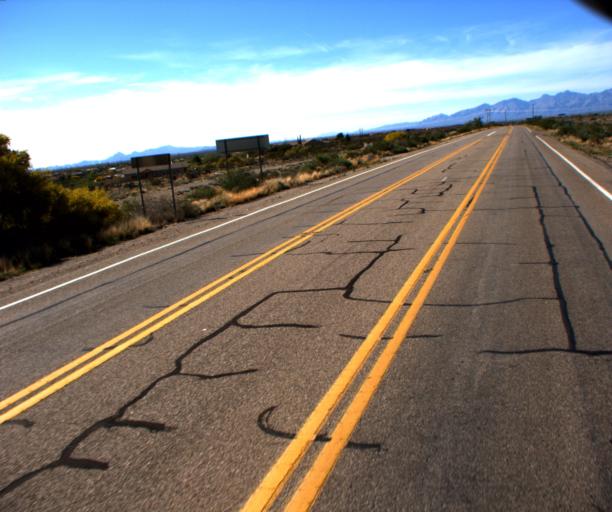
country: US
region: Arizona
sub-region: Pima County
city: Vail
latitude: 31.9985
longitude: -110.6871
